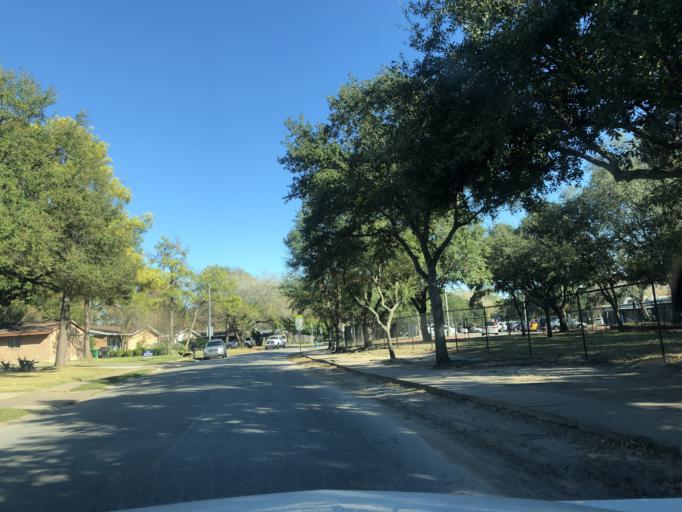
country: US
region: Texas
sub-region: Harris County
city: Bellaire
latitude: 29.6984
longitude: -95.5025
